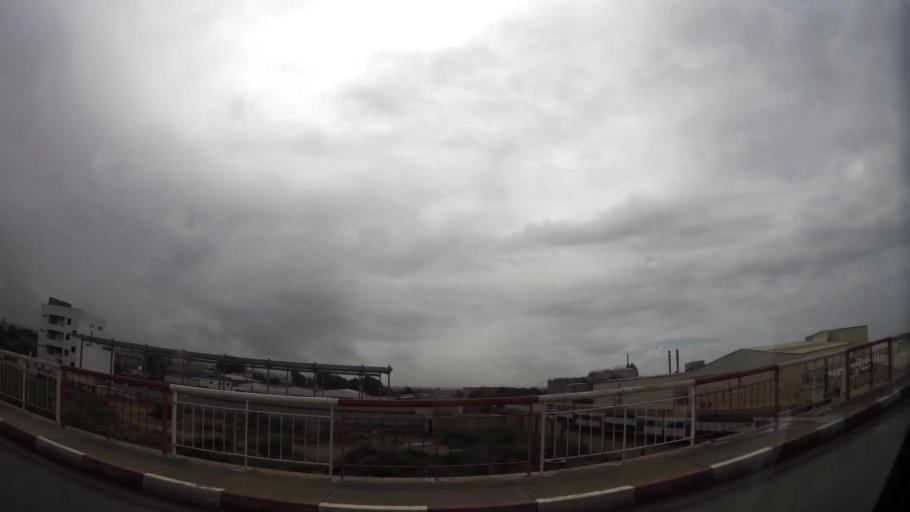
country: MA
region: Grand Casablanca
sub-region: Mediouna
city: Tit Mellil
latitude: 33.6335
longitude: -7.4708
